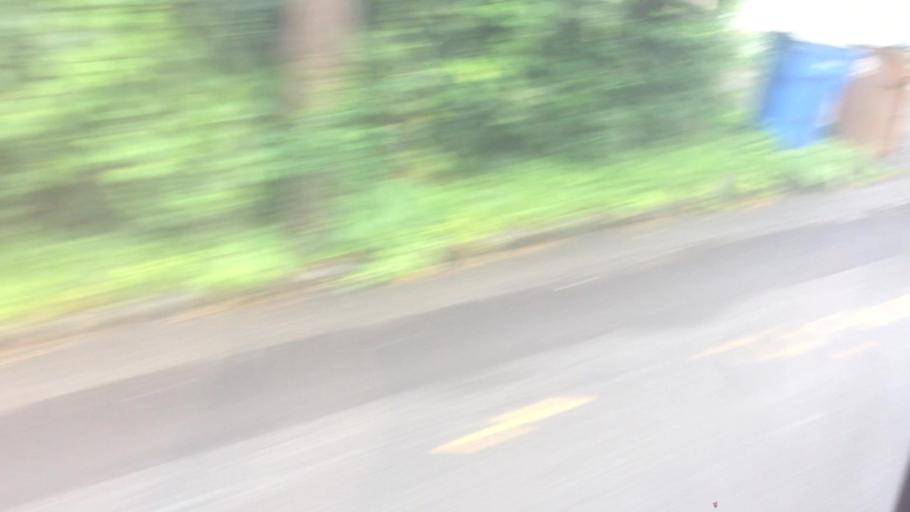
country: US
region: New York
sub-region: Ulster County
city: Kingston
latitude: 41.9388
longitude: -74.0009
